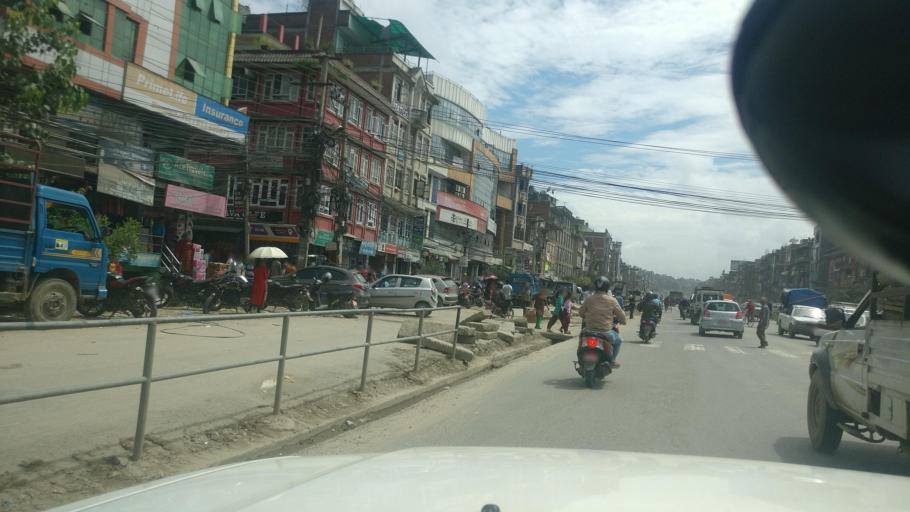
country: NP
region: Central Region
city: Banepa
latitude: 27.6307
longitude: 85.5215
